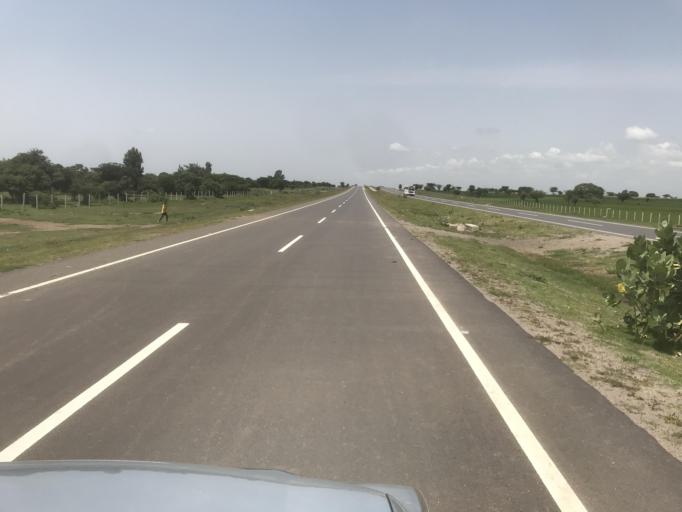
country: ET
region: Oromiya
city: Mojo
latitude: 8.2731
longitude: 38.9096
